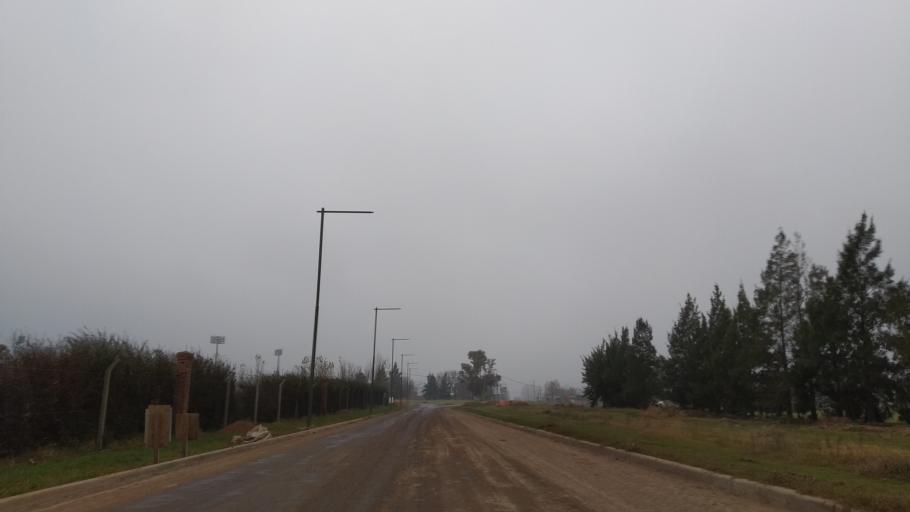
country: AR
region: Santa Fe
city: Funes
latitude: -32.9409
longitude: -60.7645
